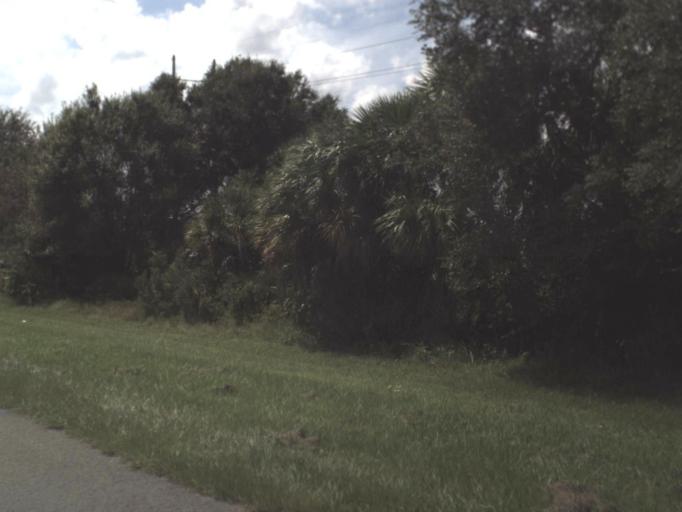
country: US
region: Florida
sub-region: Collier County
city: Immokalee
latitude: 26.3497
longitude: -81.3436
